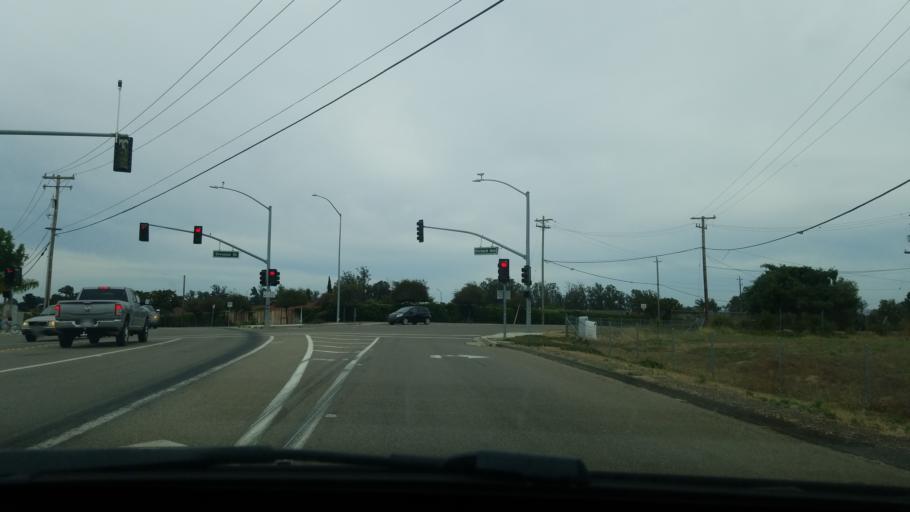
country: US
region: California
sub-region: San Luis Obispo County
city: Nipomo
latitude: 35.0223
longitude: -120.4891
